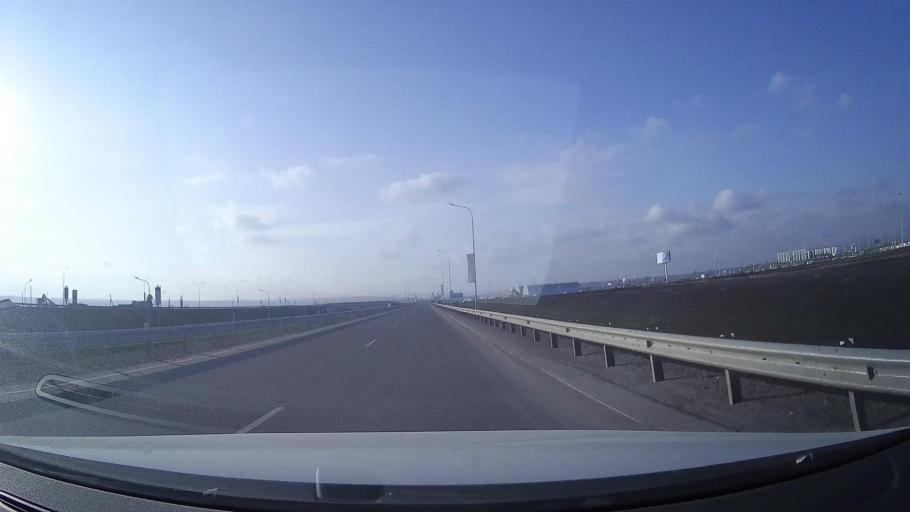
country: RU
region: Rostov
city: Grushevskaya
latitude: 47.4850
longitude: 39.9319
